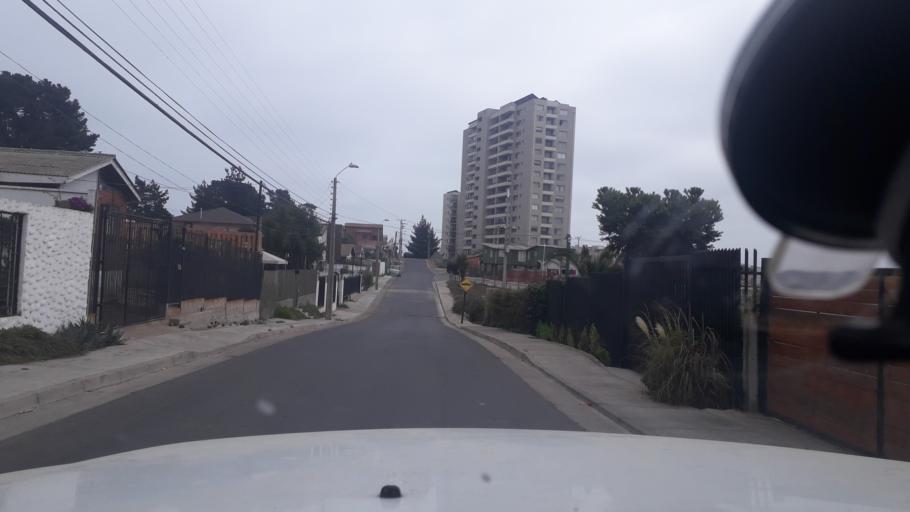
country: CL
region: Valparaiso
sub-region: Provincia de Valparaiso
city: Vina del Mar
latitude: -32.9380
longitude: -71.5315
